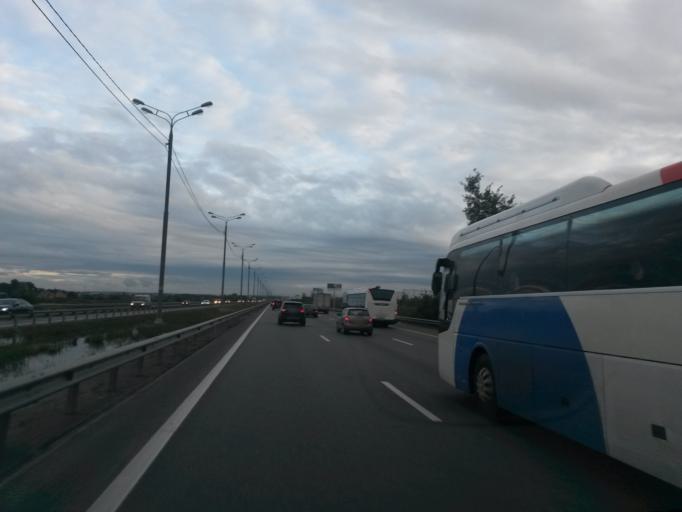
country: RU
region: Moskovskaya
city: Yam
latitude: 55.5046
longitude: 37.7229
